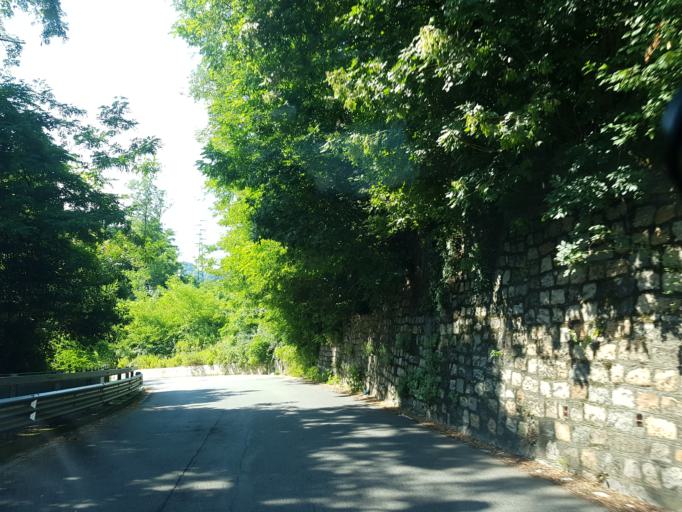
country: IT
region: Liguria
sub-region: Provincia di Genova
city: Manesseno
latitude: 44.4742
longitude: 8.9062
